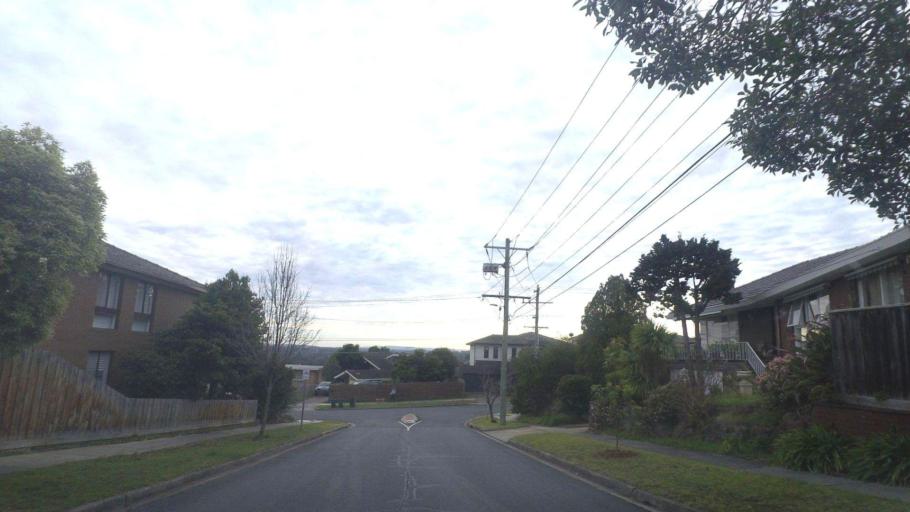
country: AU
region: Victoria
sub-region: Manningham
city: Templestowe Lower
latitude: -37.7618
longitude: 145.1054
